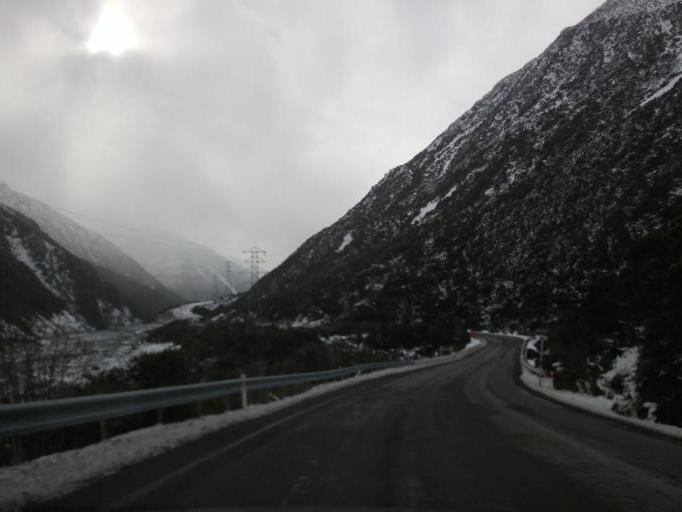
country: NZ
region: West Coast
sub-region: Grey District
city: Greymouth
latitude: -42.8959
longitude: 171.5586
